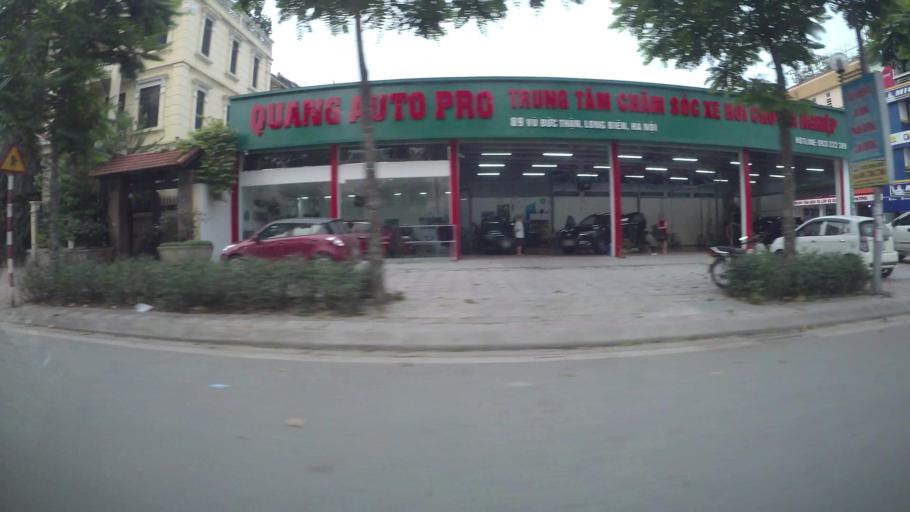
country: VN
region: Ha Noi
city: Hoan Kiem
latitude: 21.0510
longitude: 105.8948
